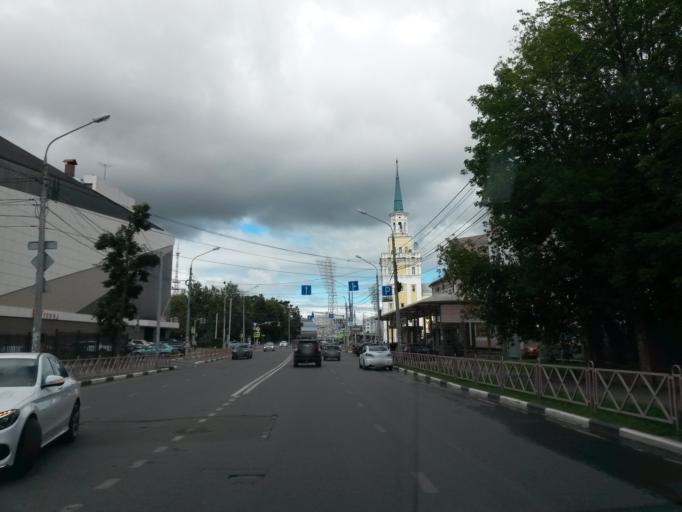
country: RU
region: Jaroslavl
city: Yaroslavl
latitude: 57.6249
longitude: 39.8680
